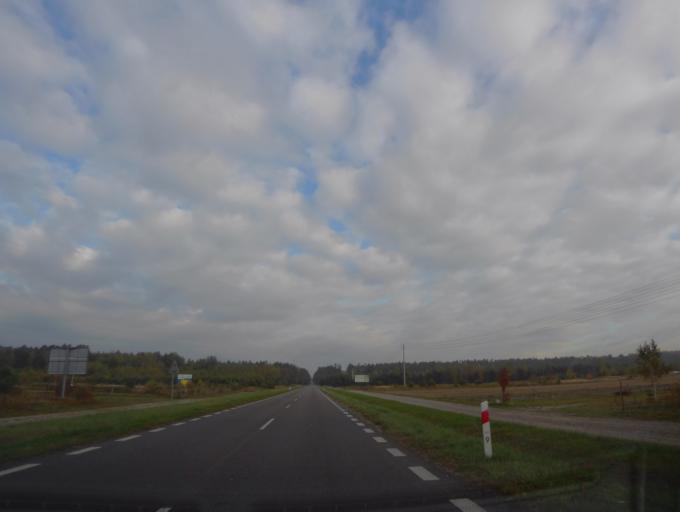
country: PL
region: Lublin Voivodeship
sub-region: Powiat bilgorajski
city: Bilgoraj
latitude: 50.5815
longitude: 22.6849
